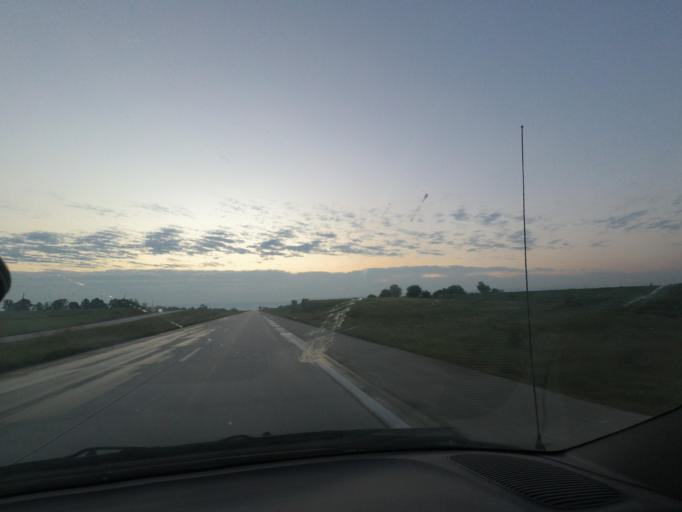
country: US
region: Missouri
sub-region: Linn County
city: Marceline
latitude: 39.7649
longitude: -92.7812
